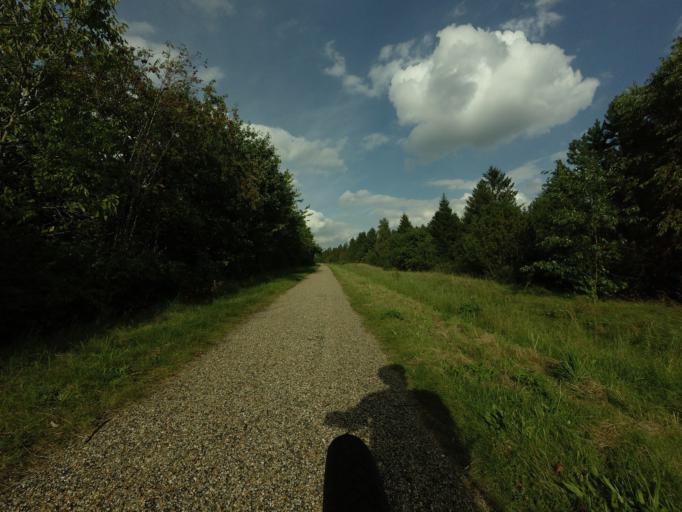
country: DK
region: Central Jutland
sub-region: Herning Kommune
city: Sunds
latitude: 56.2412
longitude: 9.0957
